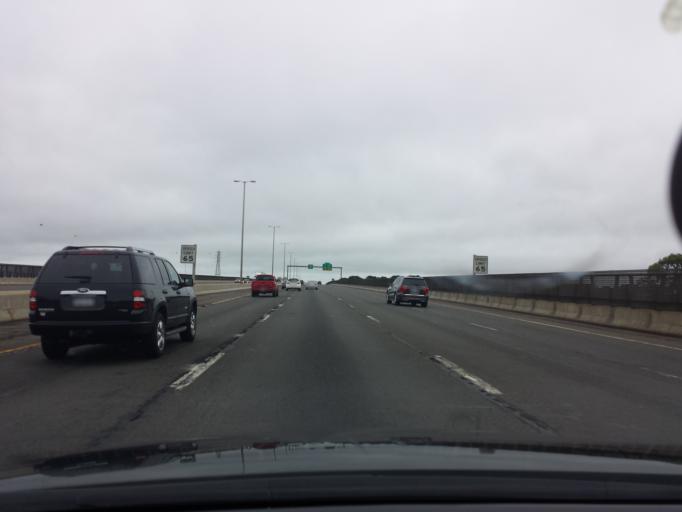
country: US
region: Connecticut
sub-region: Middlesex County
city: Old Saybrook Center
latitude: 41.3181
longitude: -72.3522
